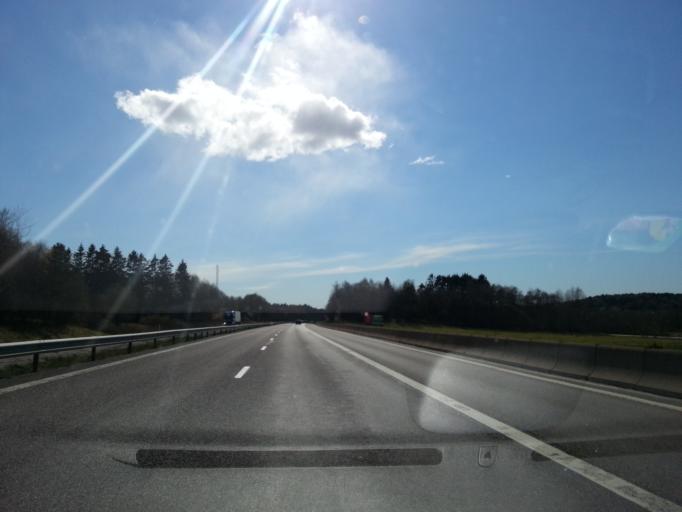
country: SE
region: Vaestra Goetaland
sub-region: Stenungsunds Kommun
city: Stora Hoga
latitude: 58.0550
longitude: 11.8746
